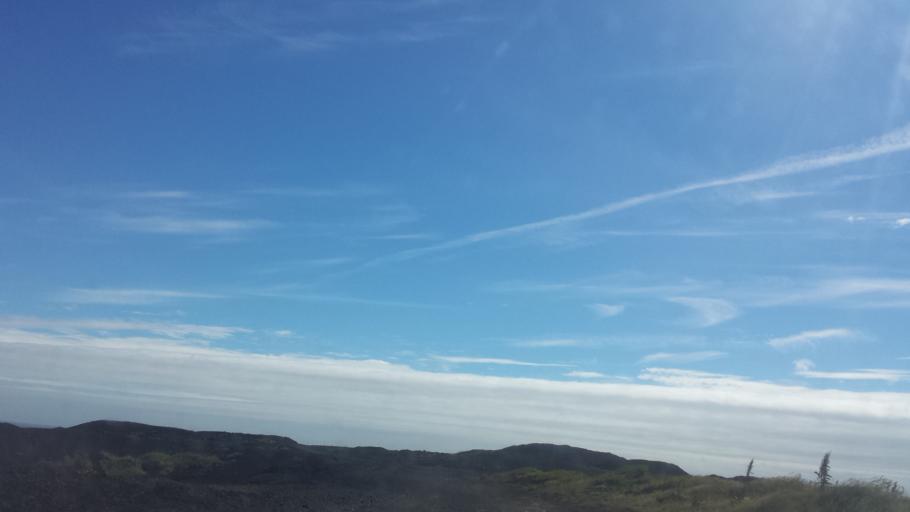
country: IS
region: South
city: Vestmannaeyjar
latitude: 63.4386
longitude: -20.2409
